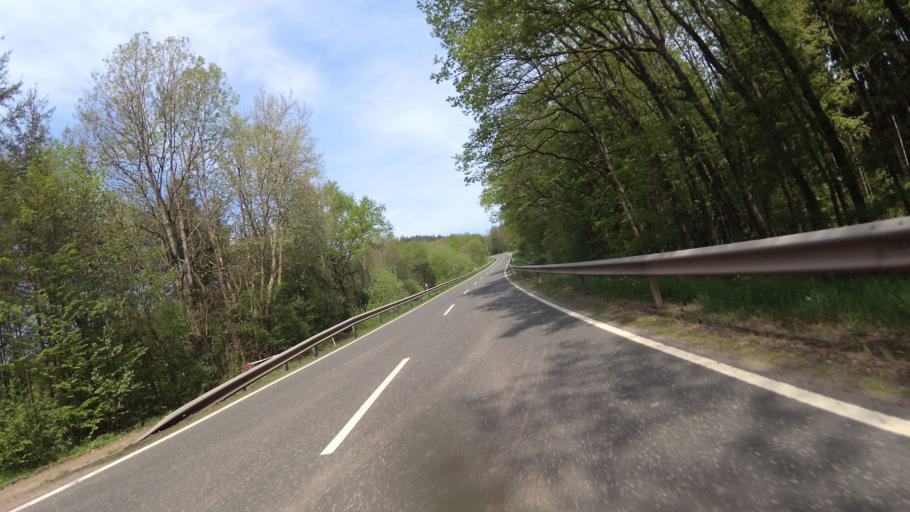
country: DE
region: Rheinland-Pfalz
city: Bausendorf
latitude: 50.0260
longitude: 6.9979
